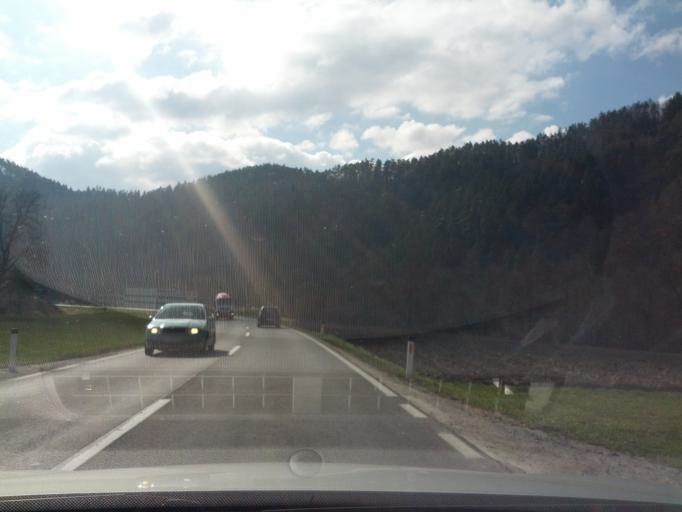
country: SI
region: Litija
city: Litija
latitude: 46.0613
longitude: 14.8145
